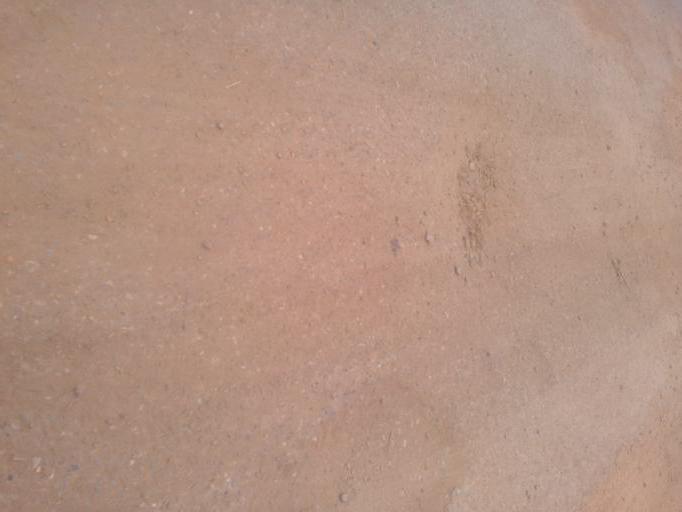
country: LA
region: Xiangkhoang
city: Muang Phonsavan
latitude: 19.6411
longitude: 103.5536
